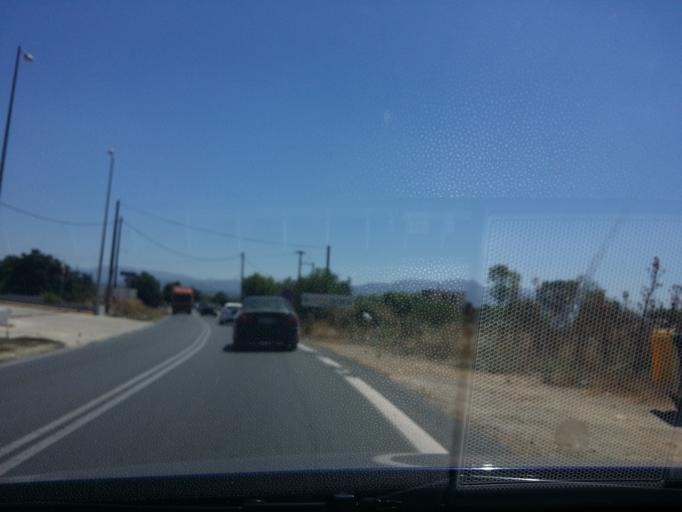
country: GR
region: Peloponnese
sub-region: Nomos Lakonias
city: Skala
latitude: 36.8444
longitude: 22.6436
